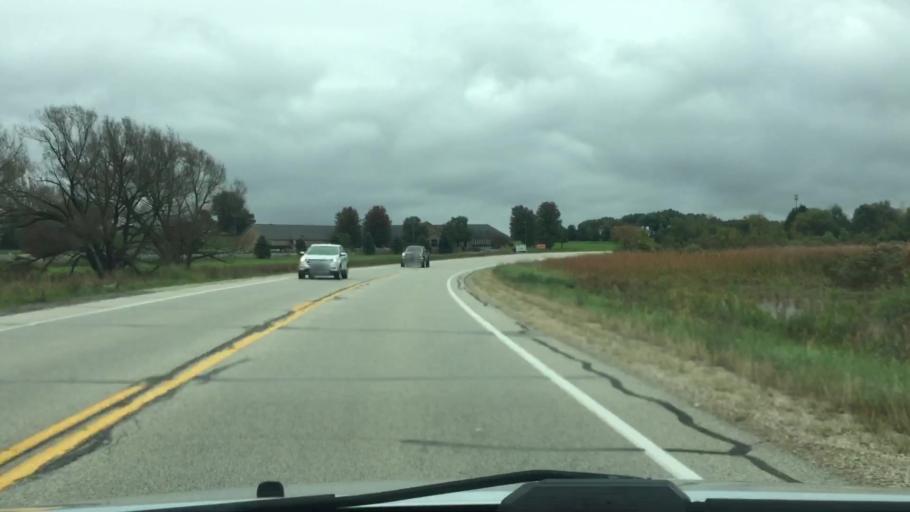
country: US
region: Wisconsin
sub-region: Walworth County
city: Elkhorn
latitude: 42.7339
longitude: -88.5444
